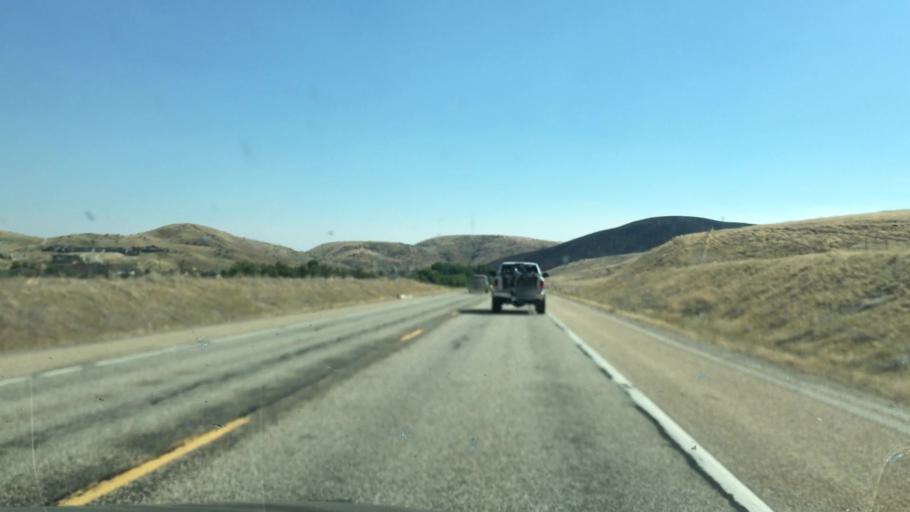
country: US
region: Idaho
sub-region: Ada County
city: Eagle
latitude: 43.7807
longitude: -116.2640
